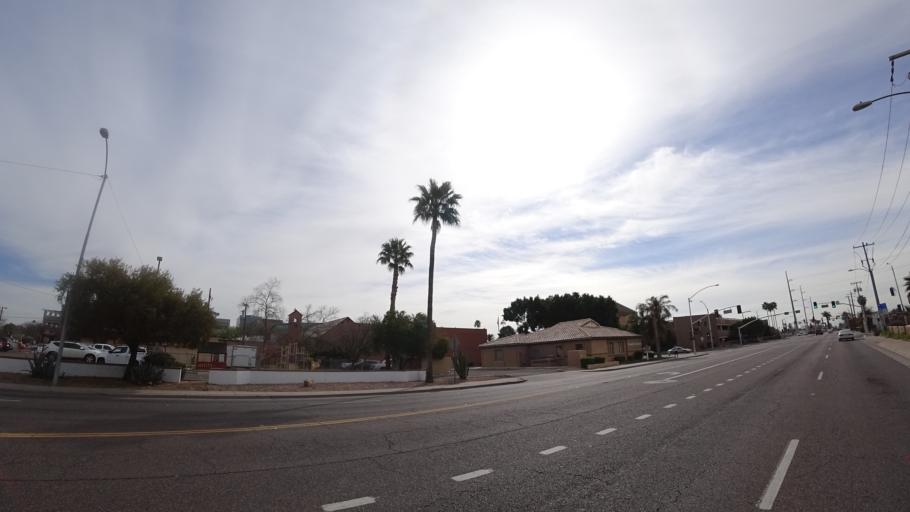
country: US
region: Arizona
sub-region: Maricopa County
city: Glendale
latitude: 33.5406
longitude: -112.1863
